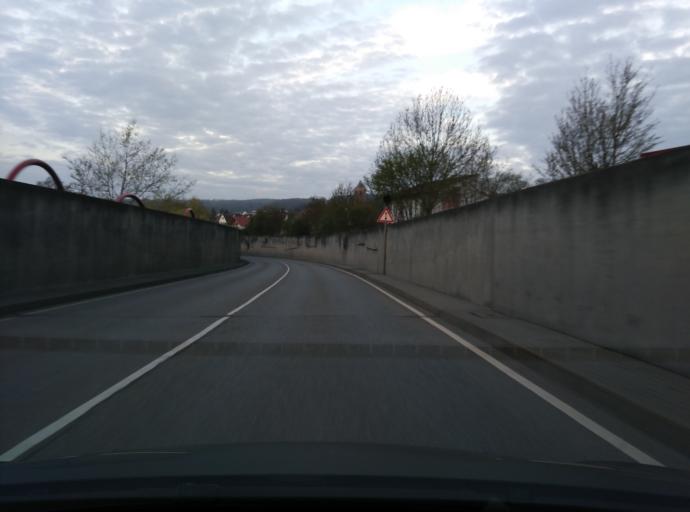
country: DE
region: Baden-Wuerttemberg
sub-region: Regierungsbezirk Stuttgart
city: Neckartailfingen
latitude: 48.6134
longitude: 9.2690
